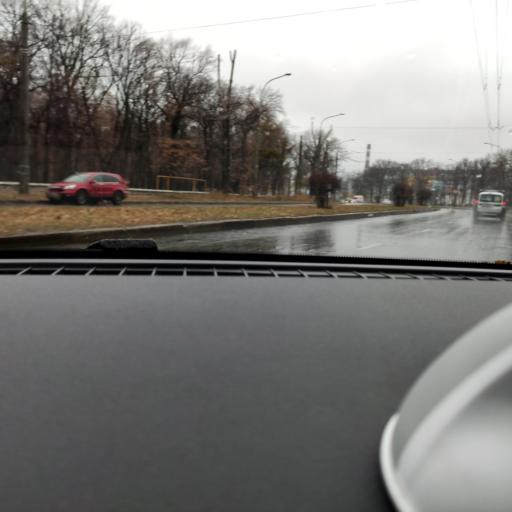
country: RU
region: Samara
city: Samara
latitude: 53.2305
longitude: 50.2051
